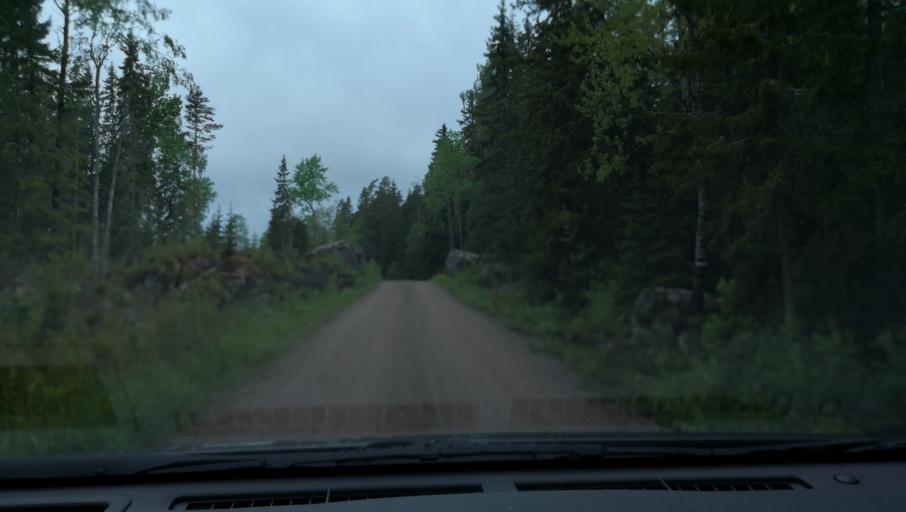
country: SE
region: Uppsala
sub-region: Enkopings Kommun
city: Orsundsbro
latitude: 59.9356
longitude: 17.3190
